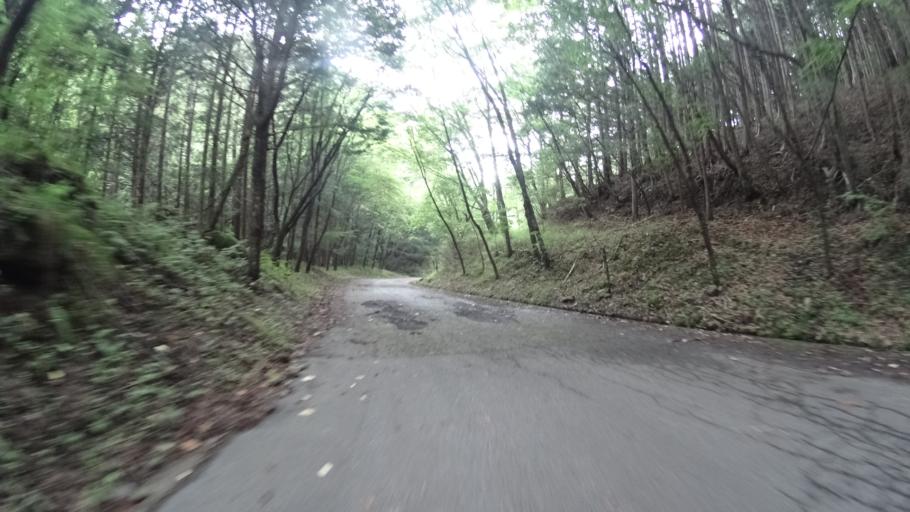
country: JP
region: Yamanashi
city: Kofu-shi
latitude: 35.8108
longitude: 138.5904
